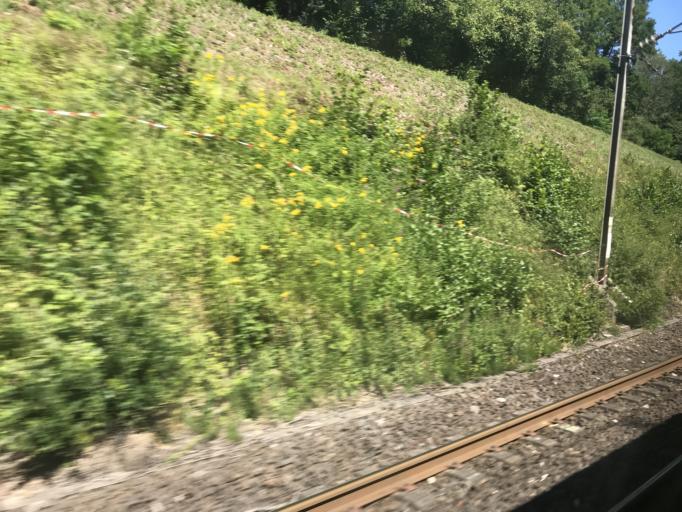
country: FR
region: Lorraine
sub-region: Departement de la Moselle
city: Niderviller
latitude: 48.7252
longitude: 7.1352
